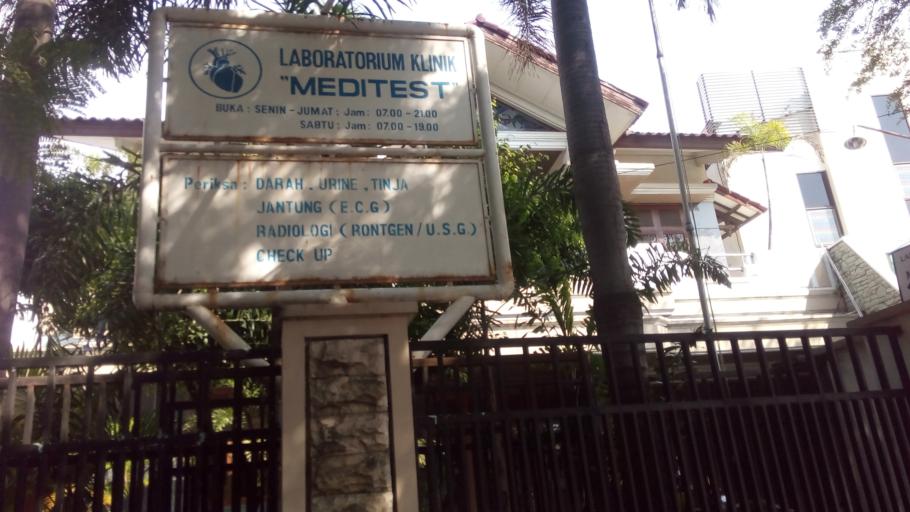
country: ID
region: Central Java
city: Semarang
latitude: -6.9951
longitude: 110.4304
